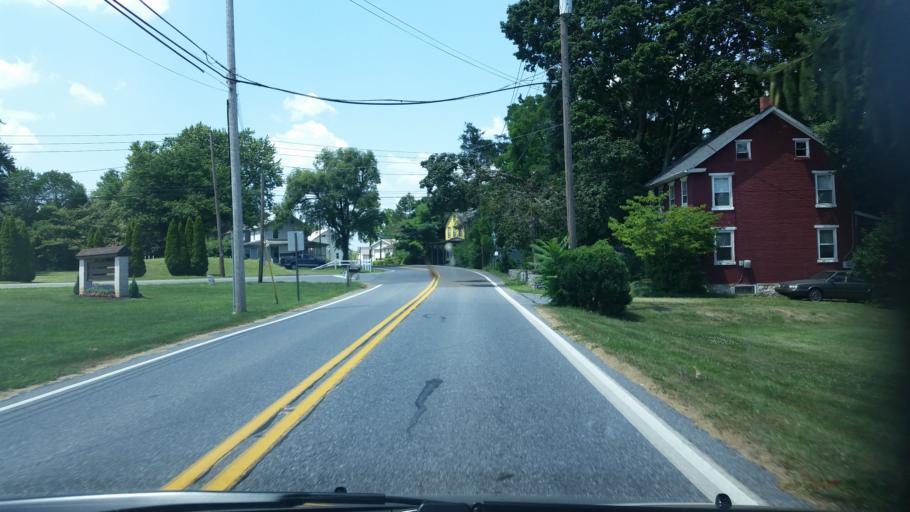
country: US
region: Pennsylvania
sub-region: Dauphin County
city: Hummelstown
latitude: 40.2865
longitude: -76.7229
